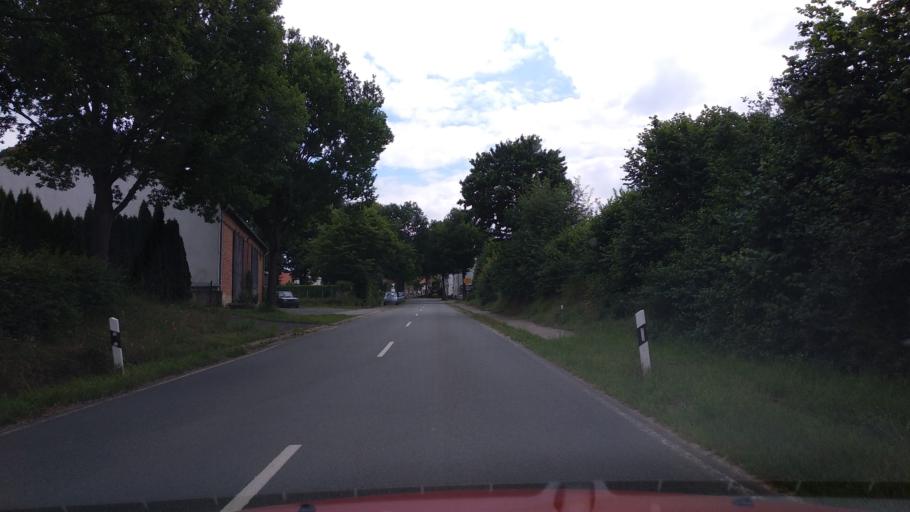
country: DE
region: North Rhine-Westphalia
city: Borgentreich
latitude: 51.5234
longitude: 9.2413
